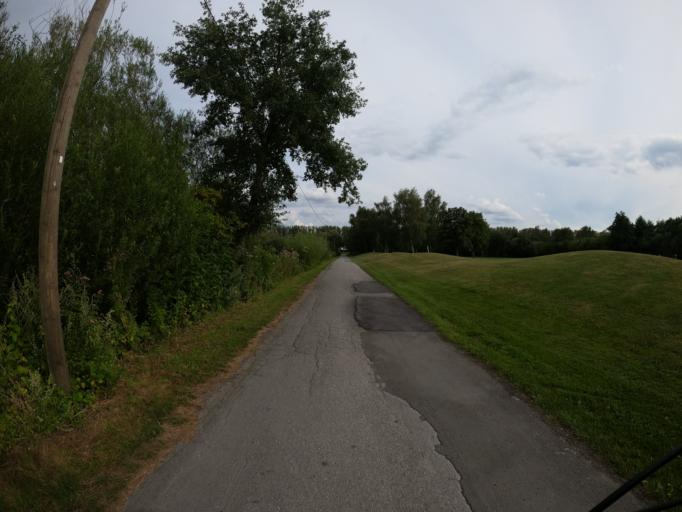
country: DE
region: North Rhine-Westphalia
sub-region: Regierungsbezirk Arnsberg
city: Lippstadt
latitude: 51.6983
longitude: 8.3247
